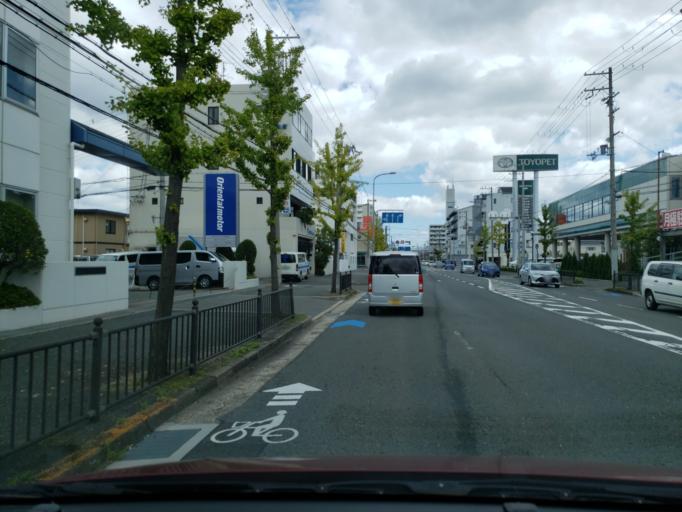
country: JP
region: Osaka
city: Toyonaka
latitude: 34.7578
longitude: 135.4708
